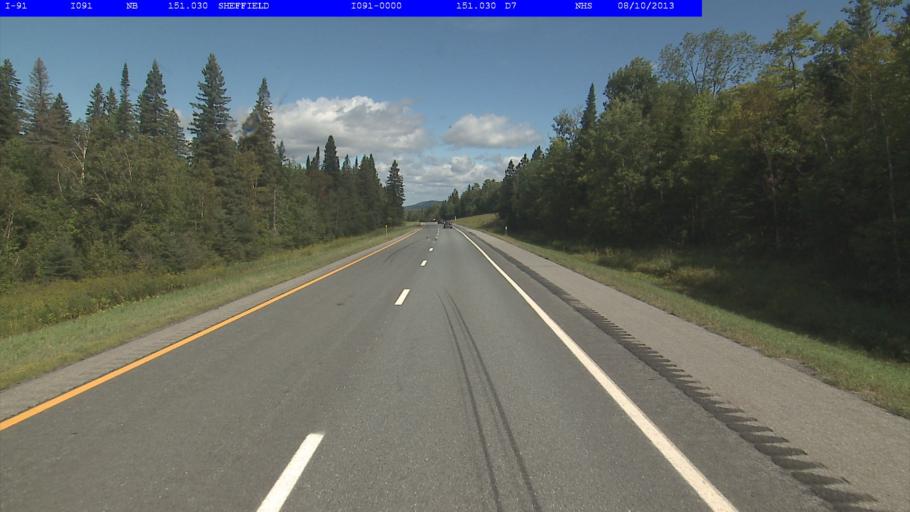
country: US
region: Vermont
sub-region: Caledonia County
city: Lyndonville
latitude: 44.6793
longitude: -72.1319
